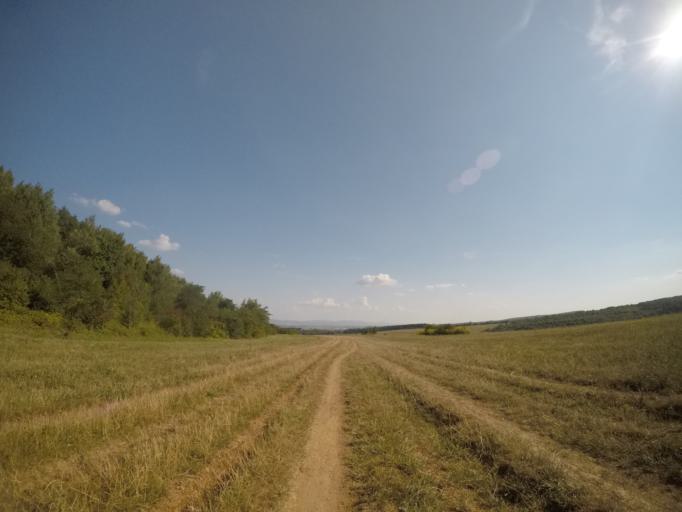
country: SK
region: Kosicky
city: Kosice
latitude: 48.7356
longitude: 21.2118
